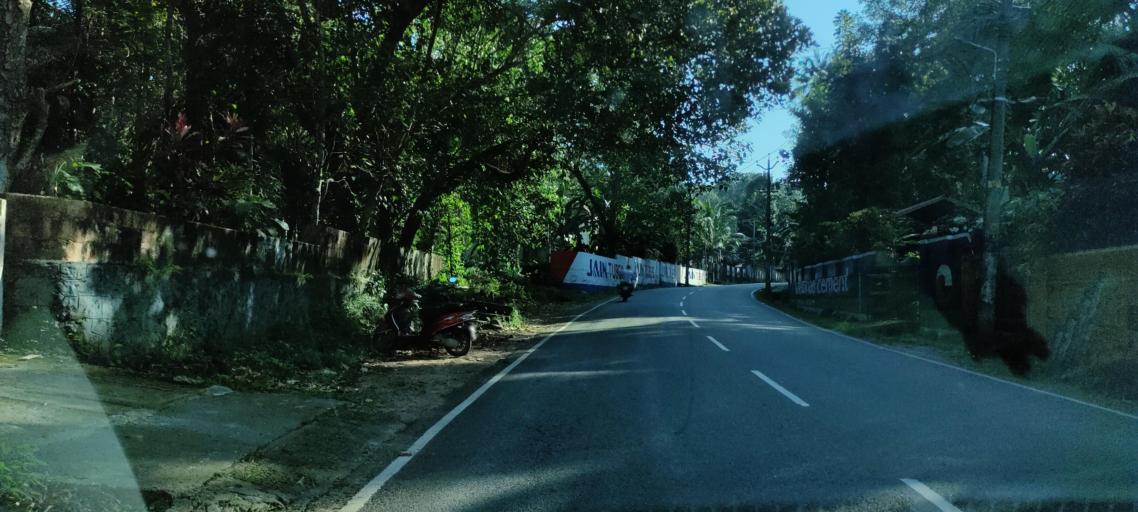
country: IN
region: Kerala
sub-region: Pattanamtitta
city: Pathanamthitta
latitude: 9.2240
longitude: 76.7525
